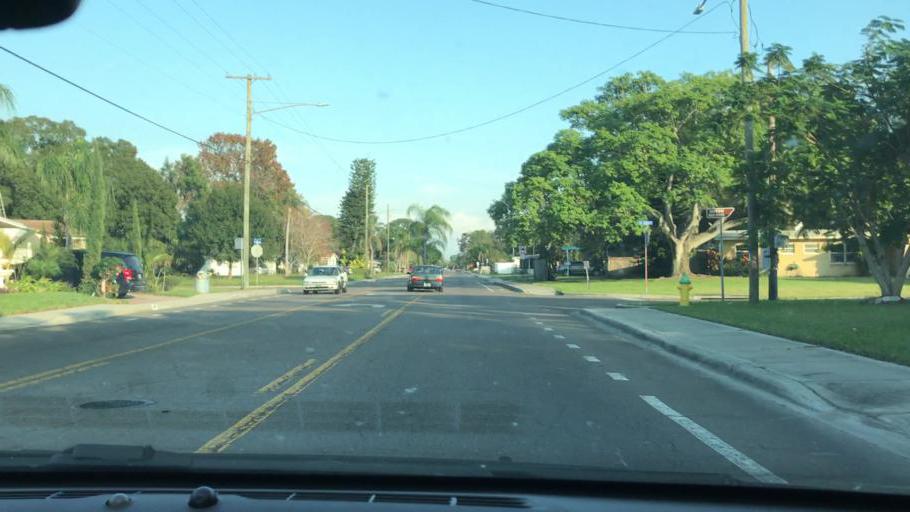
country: US
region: Florida
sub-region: Pinellas County
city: Pinellas Park
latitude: 27.8574
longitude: -82.7086
